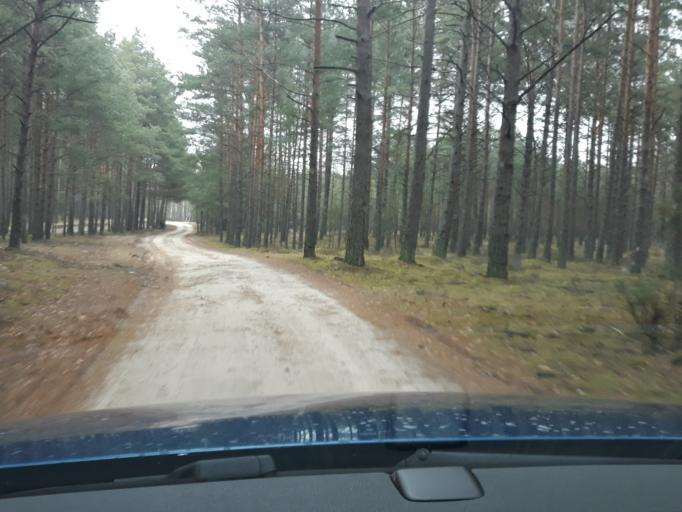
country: PL
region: Pomeranian Voivodeship
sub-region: Powiat chojnicki
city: Chojnice
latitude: 53.8592
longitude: 17.5437
